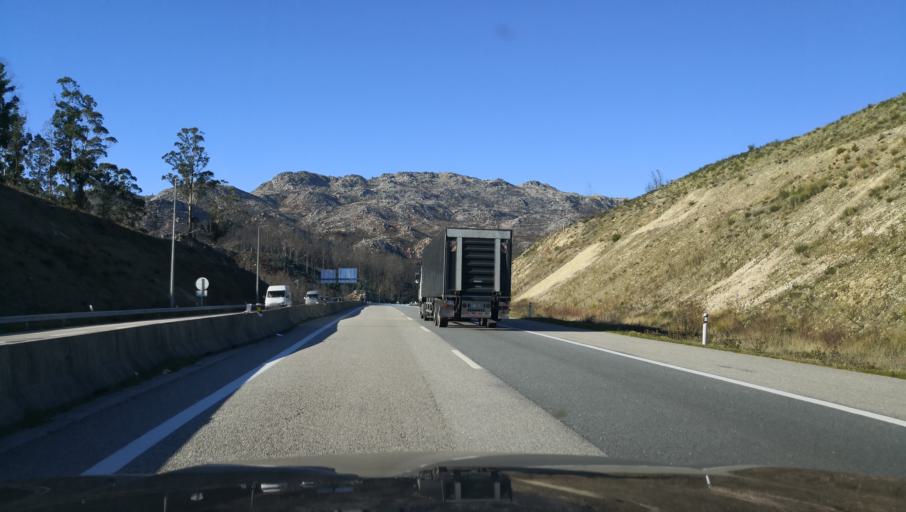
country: PT
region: Viseu
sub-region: Vouzela
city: Vouzela
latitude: 40.6509
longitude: -8.0718
